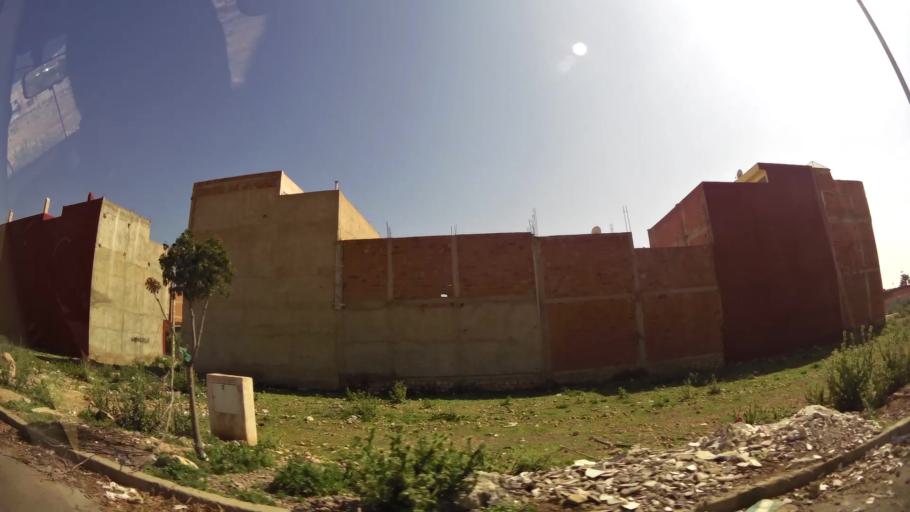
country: MA
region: Oriental
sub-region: Oujda-Angad
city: Oujda
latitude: 34.6962
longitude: -1.8729
